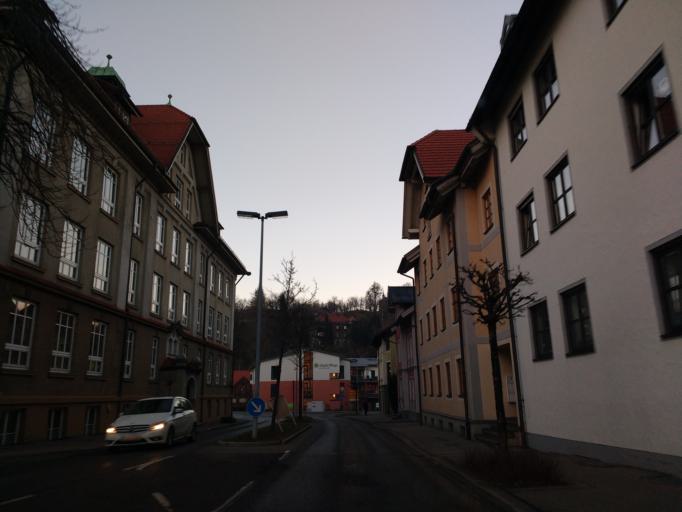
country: DE
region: Bavaria
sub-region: Swabia
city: Immenstadt im Allgau
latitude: 47.5603
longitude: 10.2212
